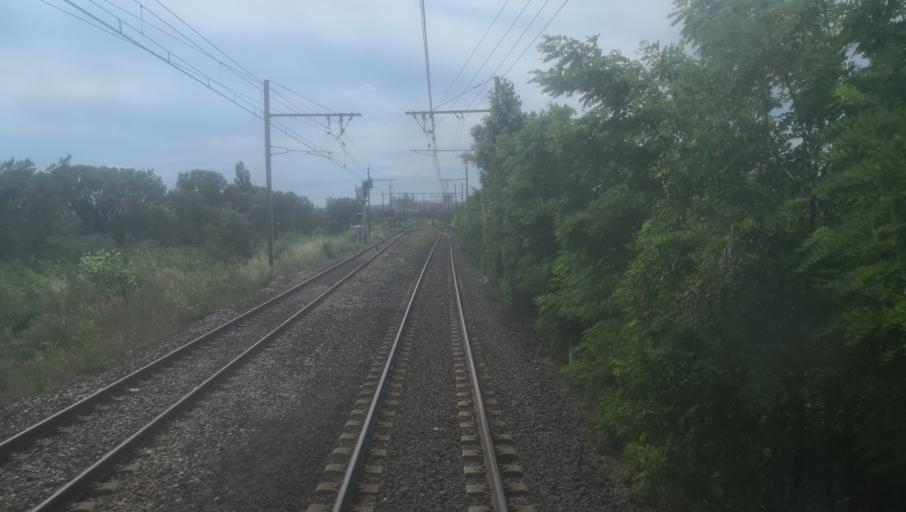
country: FR
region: Languedoc-Roussillon
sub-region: Departement du Gard
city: Beaucaire
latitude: 43.8024
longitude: 4.6453
